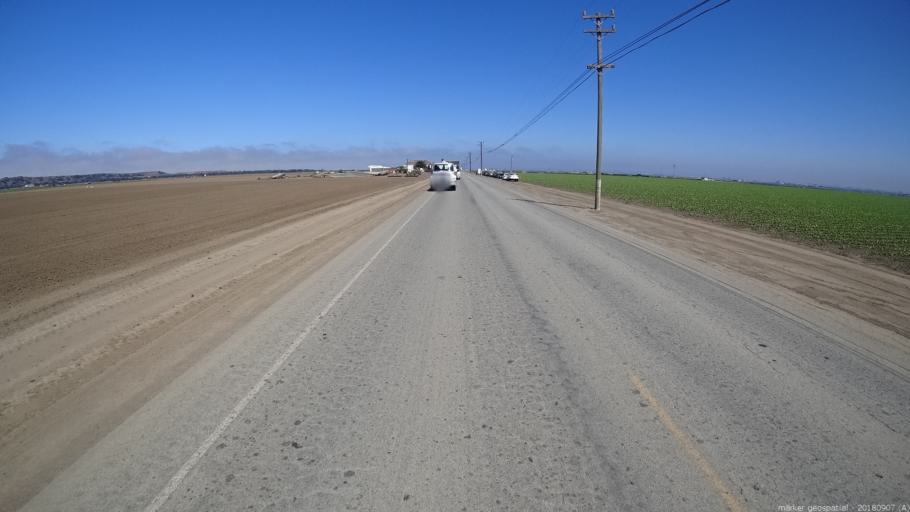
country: US
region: California
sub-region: Monterey County
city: Boronda
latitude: 36.6834
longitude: -121.7351
